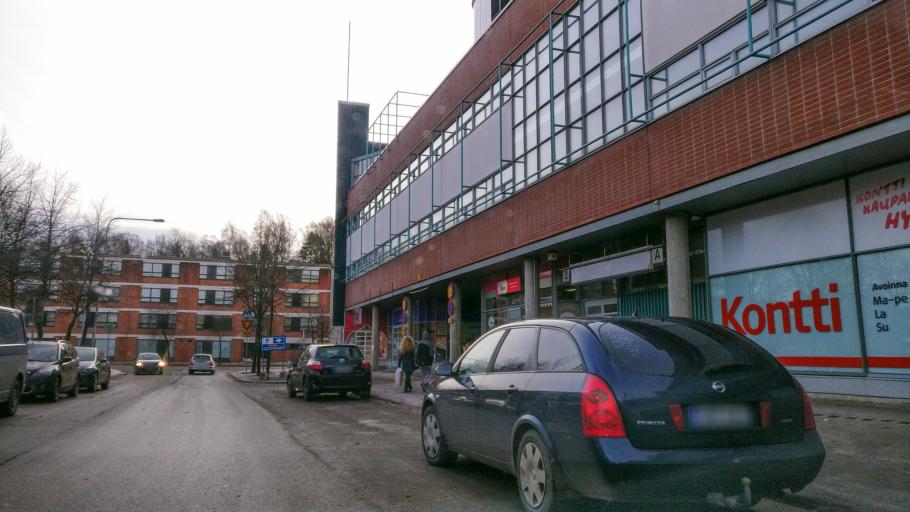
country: FI
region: Uusimaa
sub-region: Helsinki
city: Vantaa
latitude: 60.2091
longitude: 25.0841
